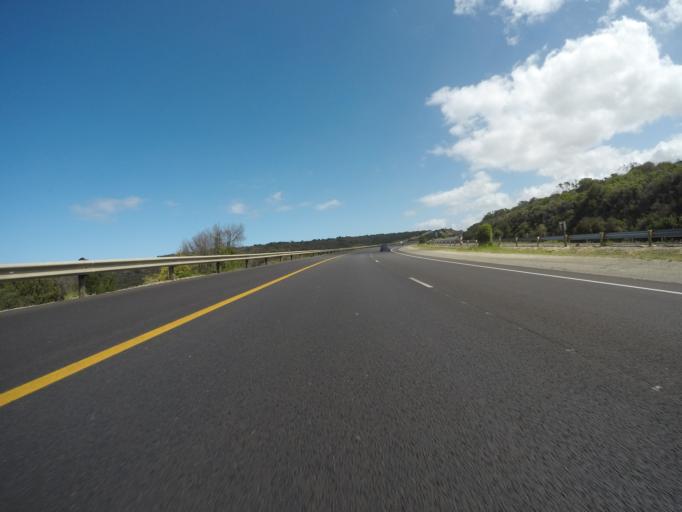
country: ZA
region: Western Cape
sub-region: Eden District Municipality
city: Mossel Bay
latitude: -34.1594
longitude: 22.0990
